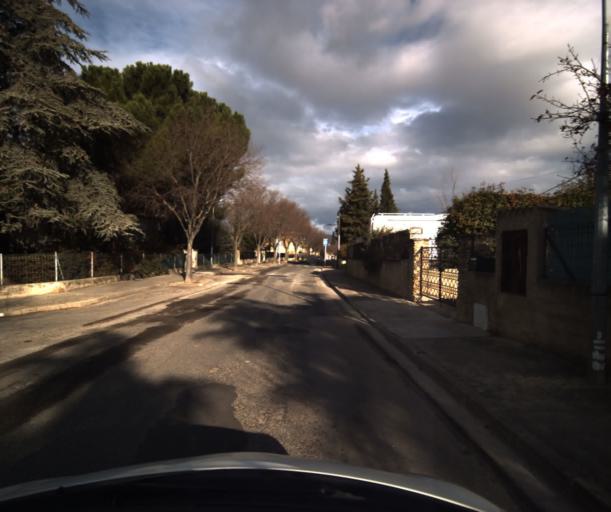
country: FR
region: Provence-Alpes-Cote d'Azur
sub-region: Departement du Vaucluse
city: Pertuis
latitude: 43.6950
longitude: 5.5171
